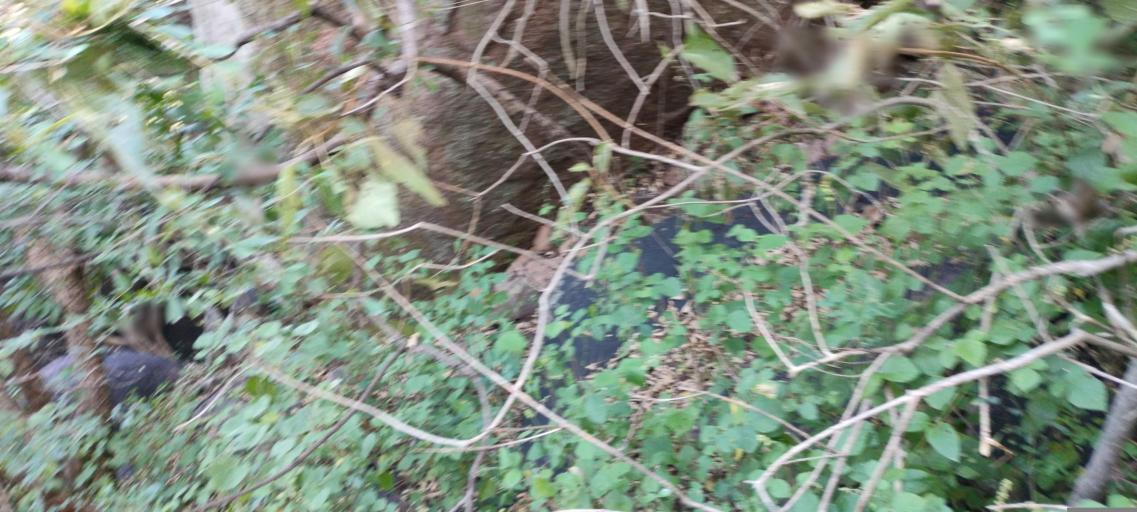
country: IN
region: Telangana
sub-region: Mahbubnagar
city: Farrukhnagar
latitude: 16.8952
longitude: 78.4950
